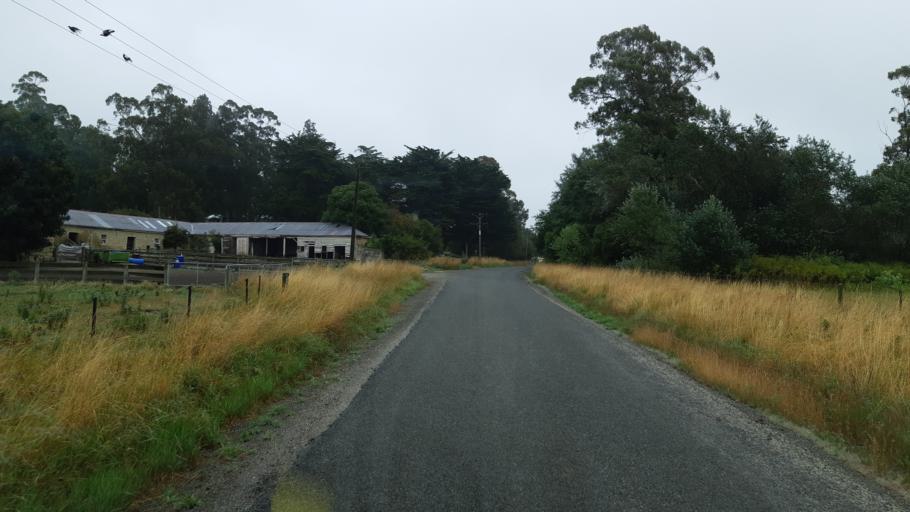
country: NZ
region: Otago
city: Oamaru
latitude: -44.9428
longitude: 170.6297
